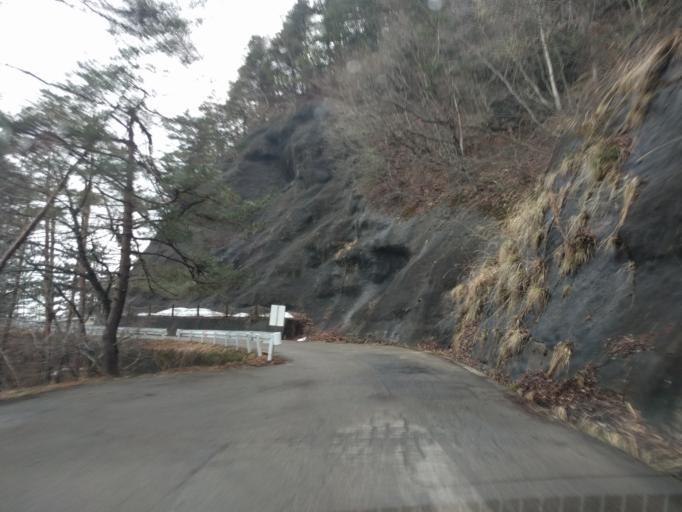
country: JP
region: Fukushima
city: Kitakata
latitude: 37.6845
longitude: 139.9280
